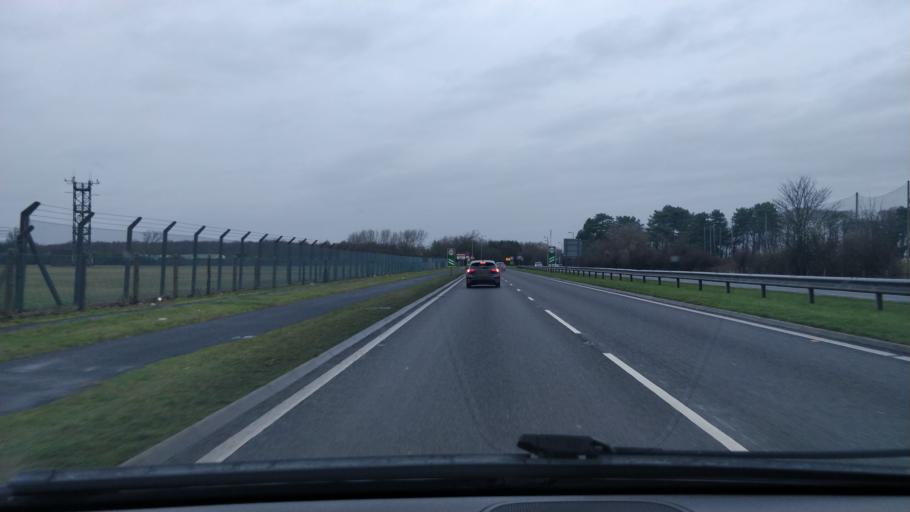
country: GB
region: England
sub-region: Sefton
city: Formby
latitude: 53.5843
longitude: -3.0450
